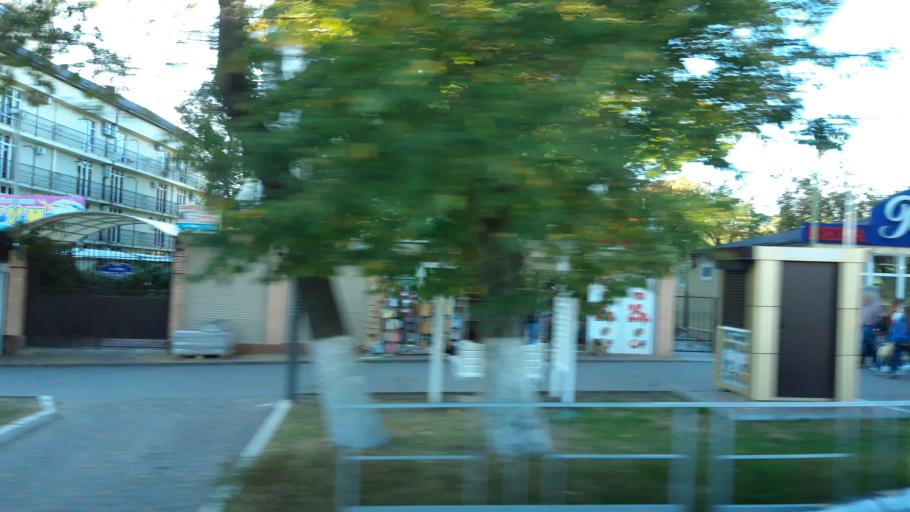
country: RU
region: Krasnodarskiy
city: Kabardinka
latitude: 44.6505
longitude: 37.9383
